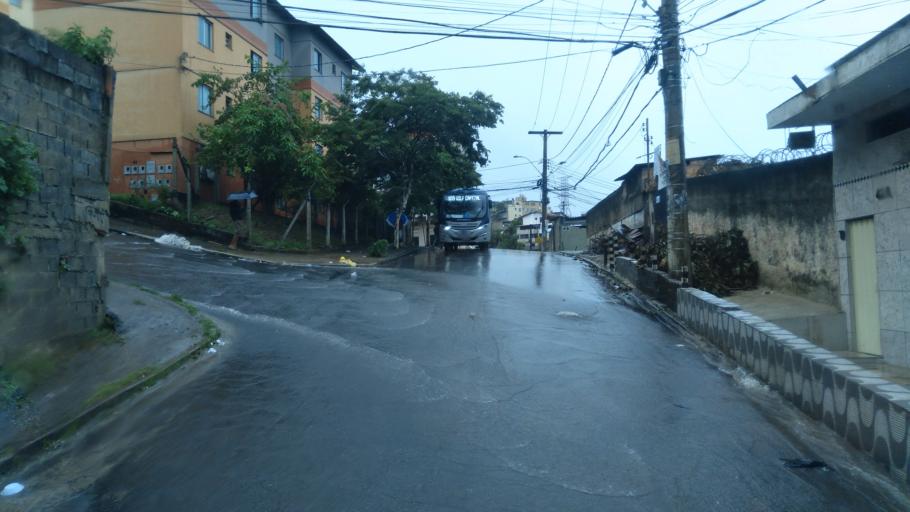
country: BR
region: Minas Gerais
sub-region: Belo Horizonte
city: Belo Horizonte
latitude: -19.9296
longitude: -43.9092
